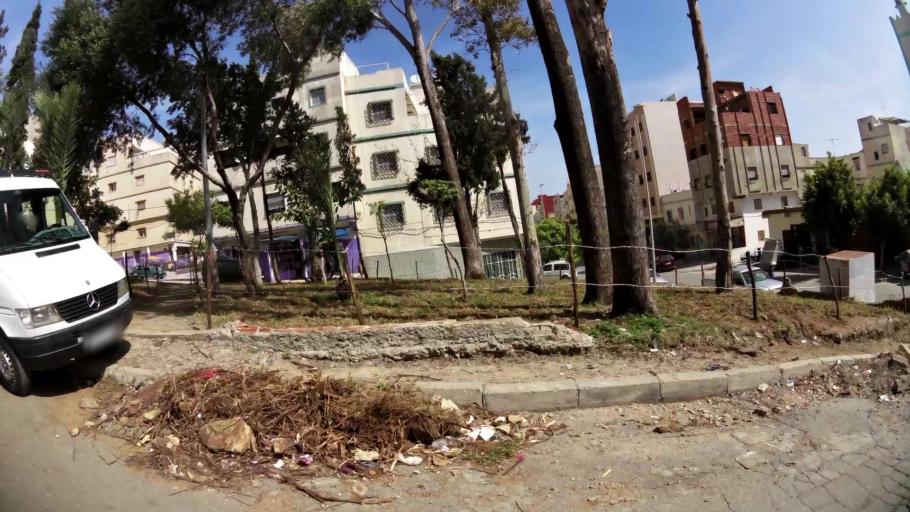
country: MA
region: Tanger-Tetouan
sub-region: Tanger-Assilah
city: Tangier
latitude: 35.7383
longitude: -5.8031
